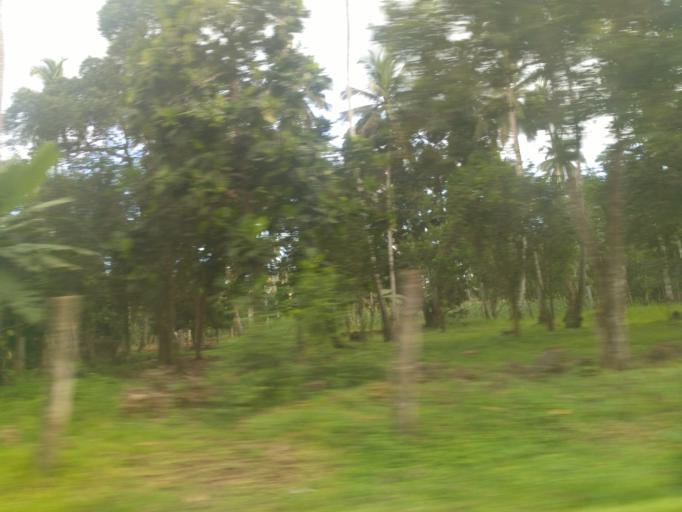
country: TZ
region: Zanzibar Central/South
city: Koani
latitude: -6.1060
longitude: 39.2896
